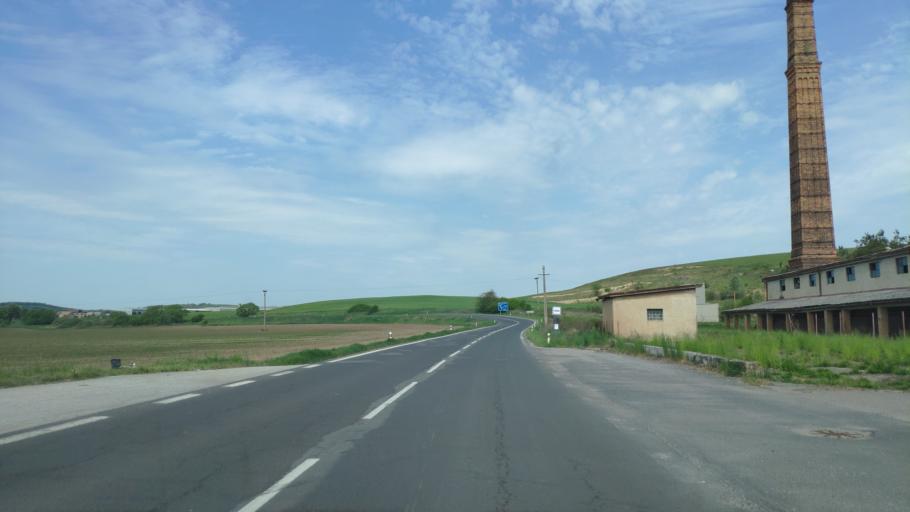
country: HU
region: Borsod-Abauj-Zemplen
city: Putnok
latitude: 48.4261
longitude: 20.3067
